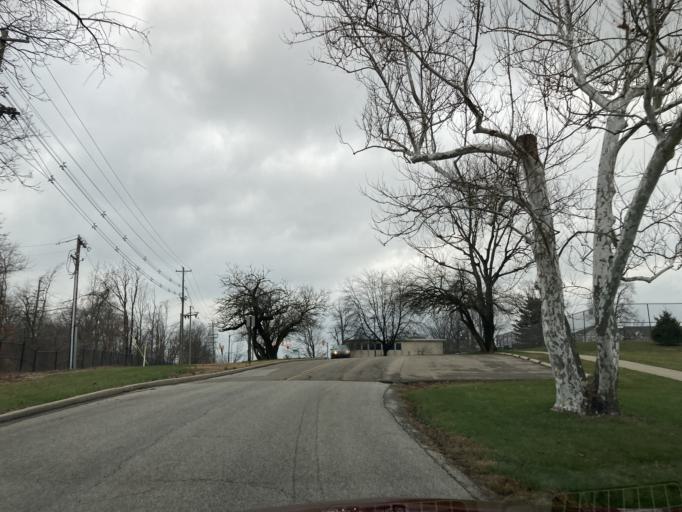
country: US
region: Indiana
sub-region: Monroe County
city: Bloomington
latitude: 39.1731
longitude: -86.5140
